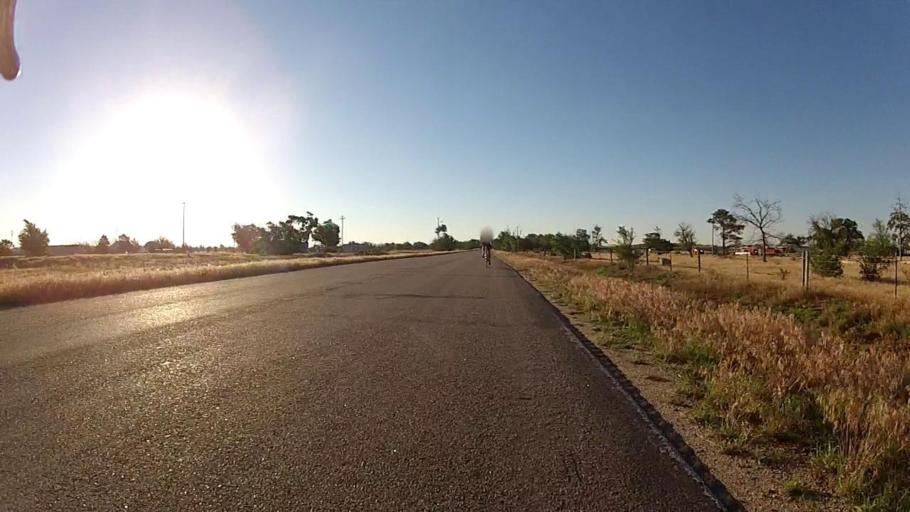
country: US
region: Kansas
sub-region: Ford County
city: Dodge City
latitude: 37.7155
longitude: -99.9339
